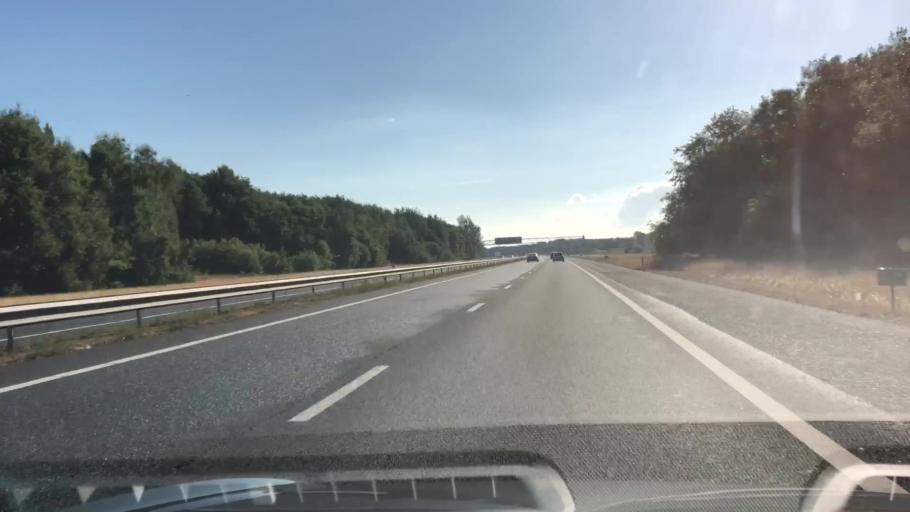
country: NL
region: Gelderland
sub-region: Gemeente Barneveld
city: Voorthuizen
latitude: 52.1702
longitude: 5.6198
